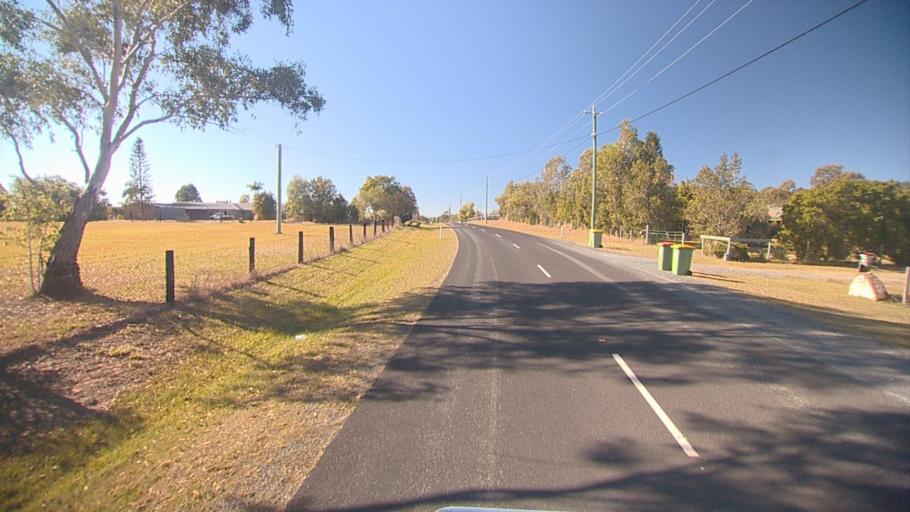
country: AU
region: Queensland
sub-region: Logan
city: North Maclean
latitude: -27.7425
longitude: 152.9477
